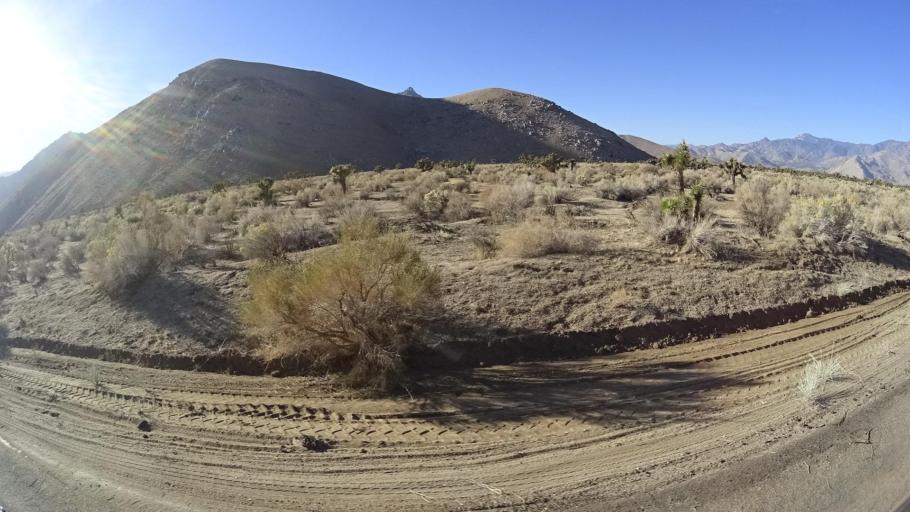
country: US
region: California
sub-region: Kern County
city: Weldon
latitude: 35.6088
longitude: -118.2427
